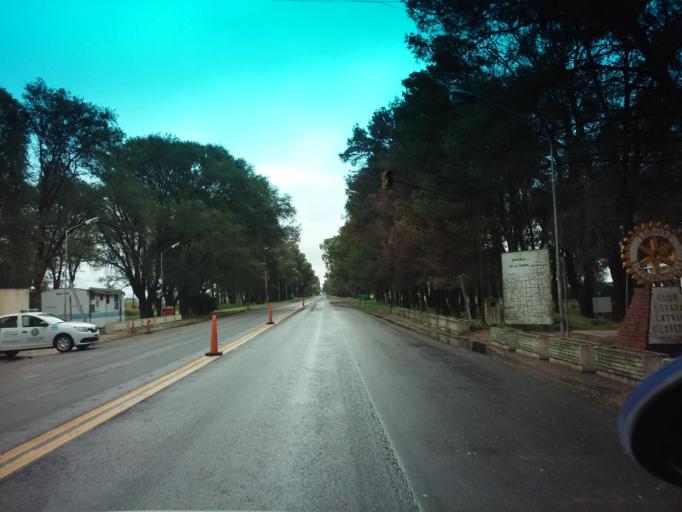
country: AR
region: La Pampa
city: Catrilo
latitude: -36.4107
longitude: -63.3866
